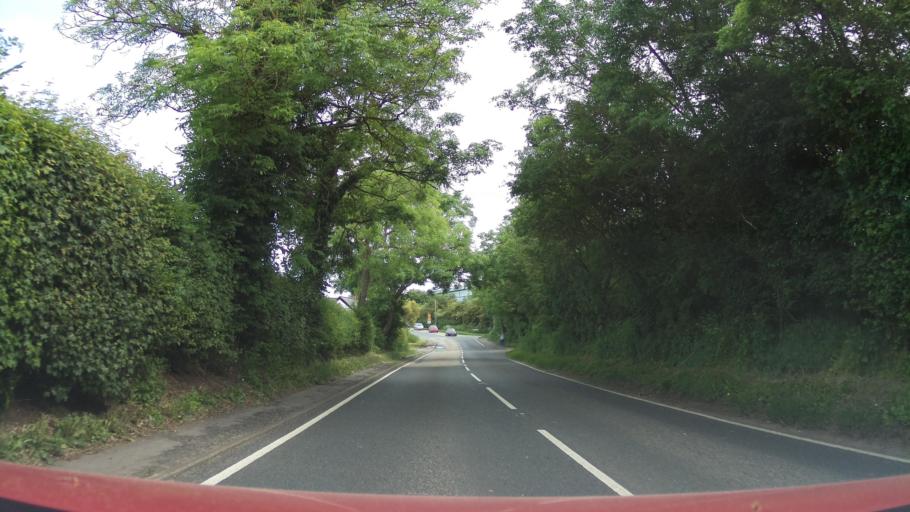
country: GB
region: England
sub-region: Worcestershire
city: Kempsey
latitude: 52.1614
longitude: -2.1606
